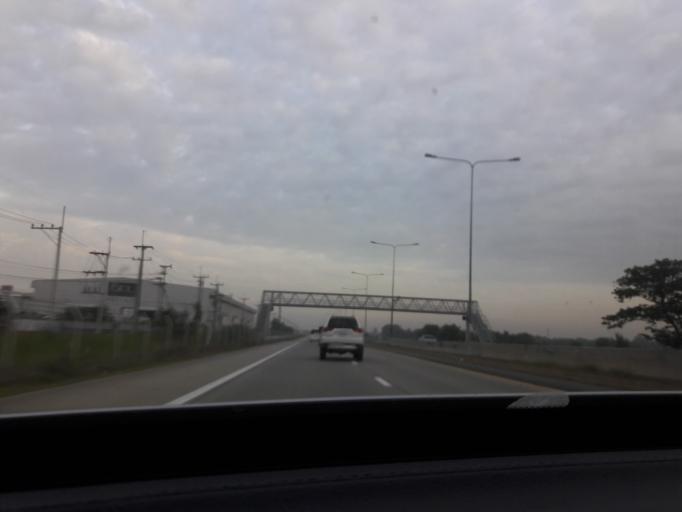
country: TH
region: Pathum Thani
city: Sam Khok
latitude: 14.1047
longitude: 100.5774
